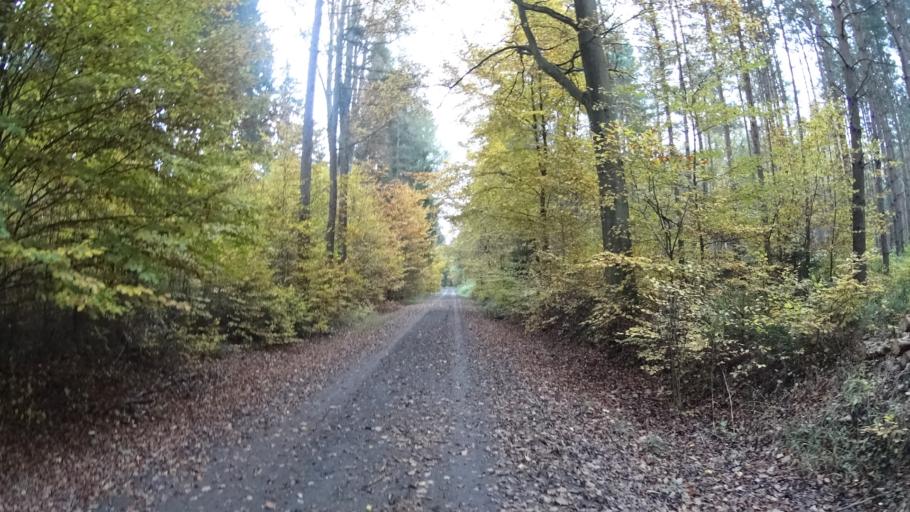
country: DE
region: Thuringia
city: Kleineutersdorf
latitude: 50.7600
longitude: 11.5764
